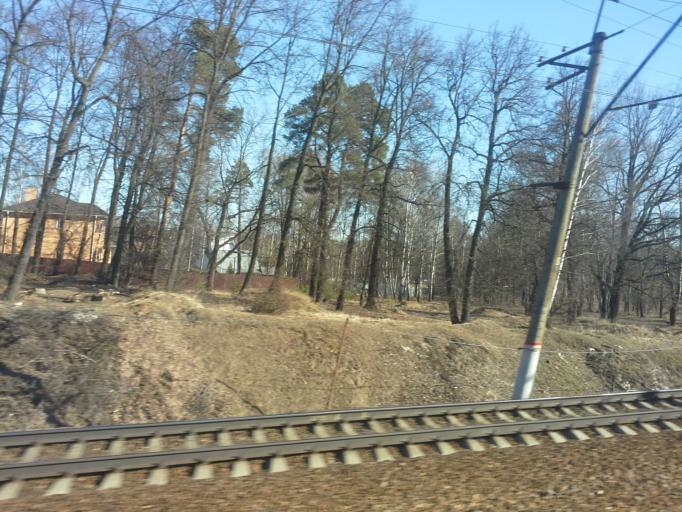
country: RU
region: Moskovskaya
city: Mamontovka
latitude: 55.9720
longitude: 37.8151
